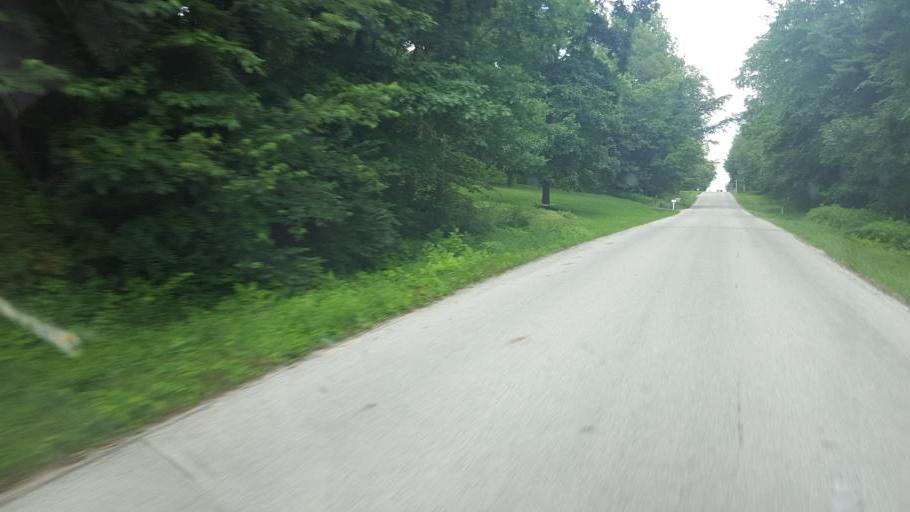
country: US
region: Ohio
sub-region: Richland County
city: Lexington
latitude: 40.7109
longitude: -82.6563
